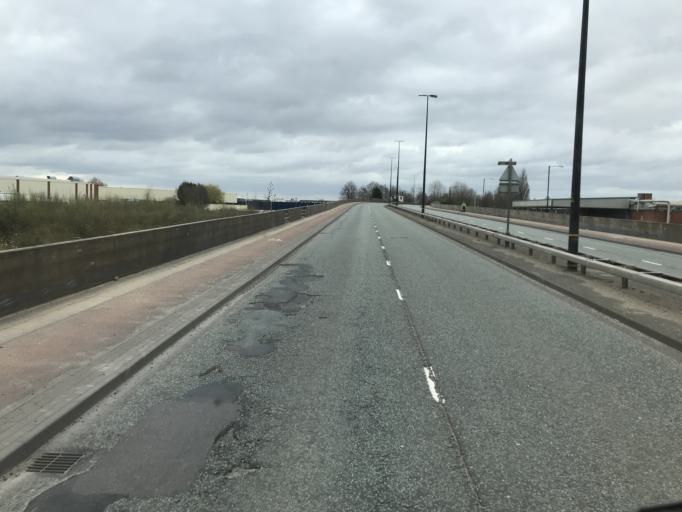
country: GB
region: England
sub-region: City and Borough of Salford
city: Eccles
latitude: 53.4796
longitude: -2.3250
